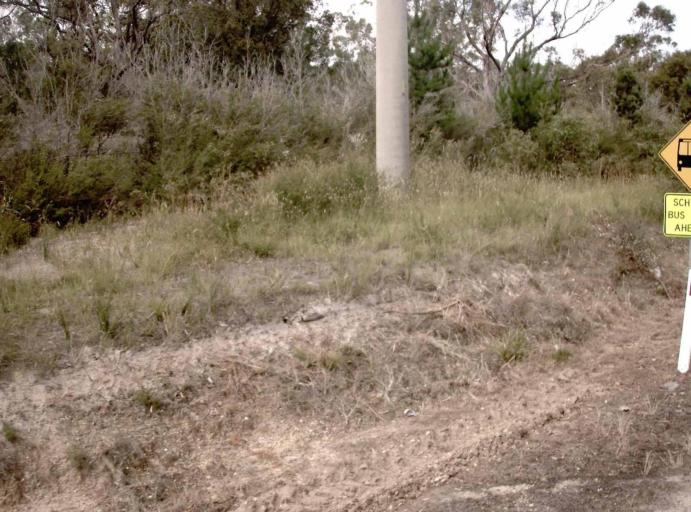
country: AU
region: Victoria
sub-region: Wellington
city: Sale
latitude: -38.2169
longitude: 147.1107
